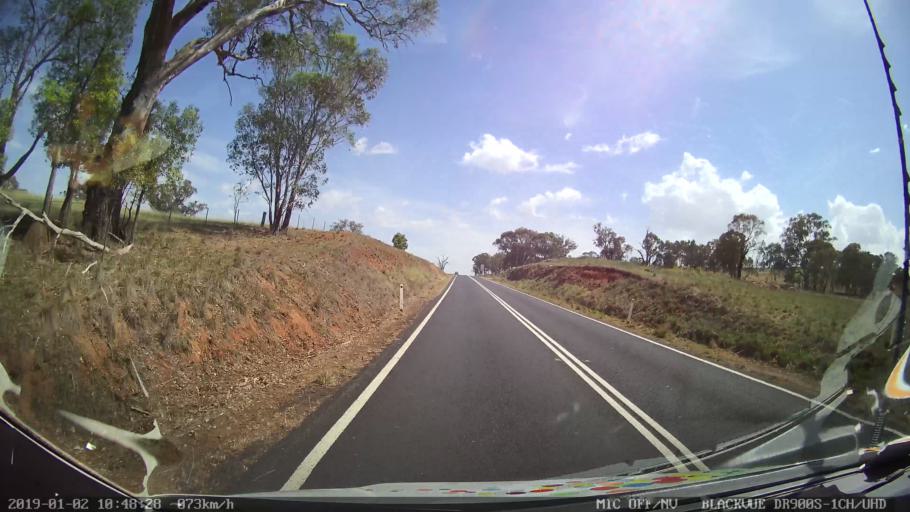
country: AU
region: New South Wales
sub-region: Cootamundra
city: Cootamundra
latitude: -34.7364
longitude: 148.2779
